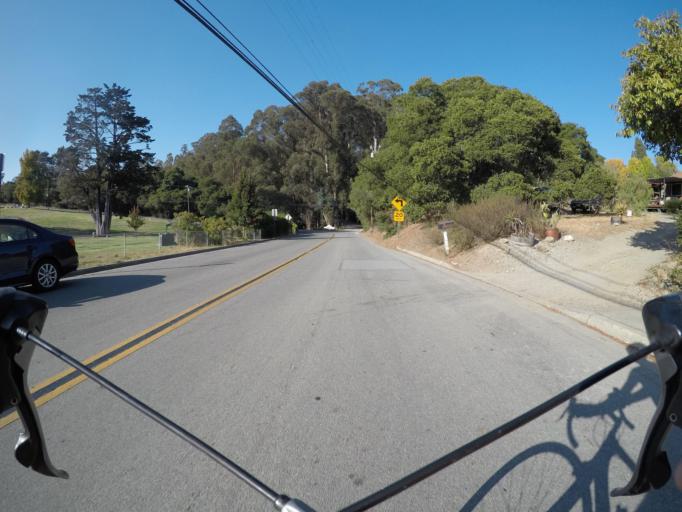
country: US
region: California
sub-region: Santa Cruz County
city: Live Oak
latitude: 36.9928
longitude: -121.9841
